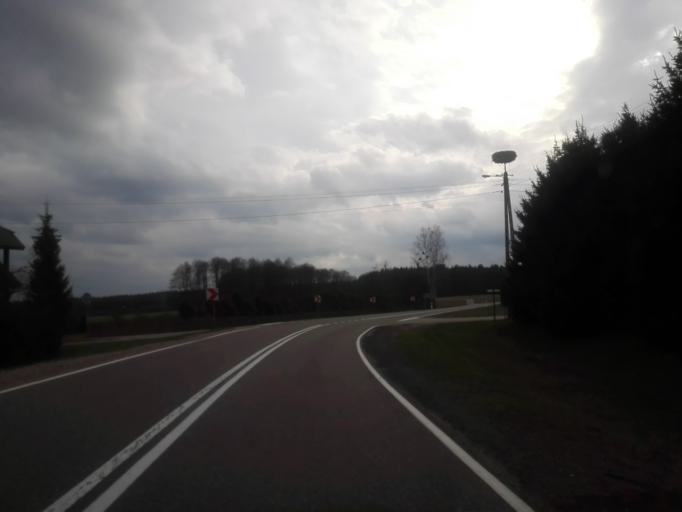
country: PL
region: Podlasie
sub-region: Powiat sejnenski
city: Krasnopol
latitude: 53.9408
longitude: 23.1829
